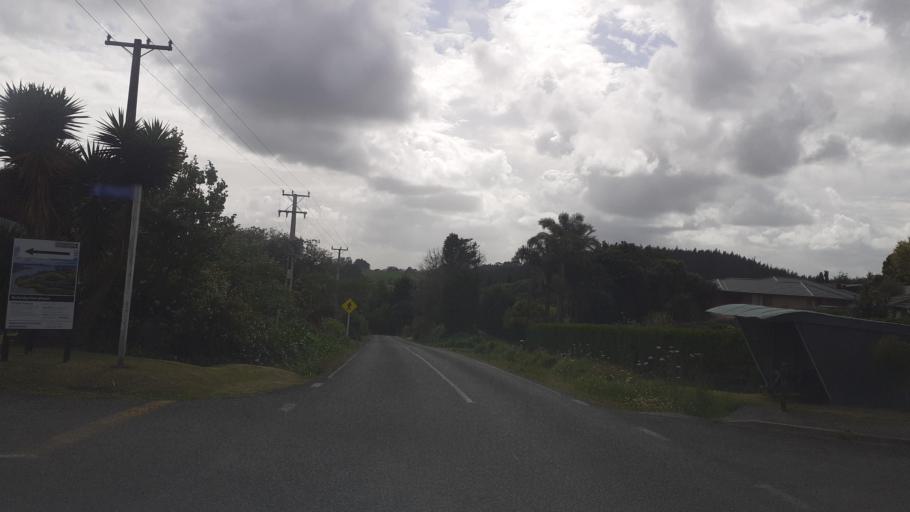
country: NZ
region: Northland
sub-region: Far North District
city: Kerikeri
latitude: -35.2176
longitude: 173.9797
